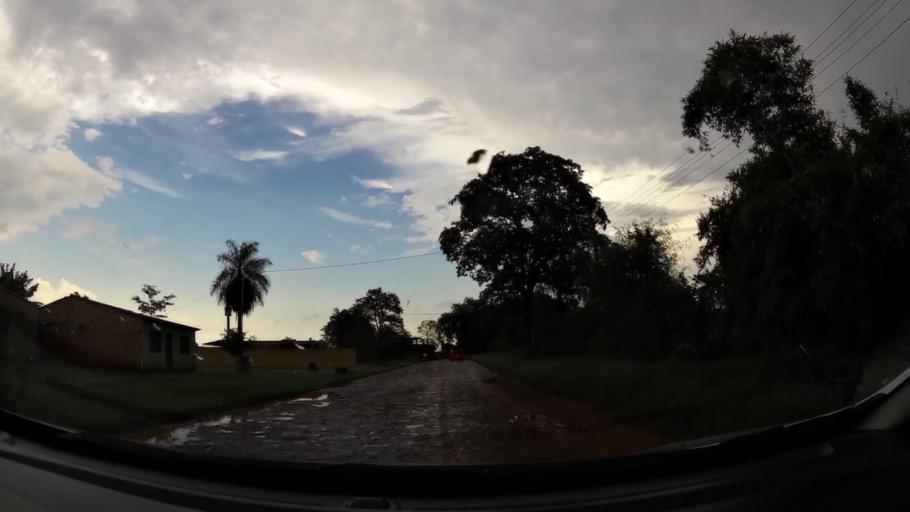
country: PY
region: Alto Parana
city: Presidente Franco
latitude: -25.5423
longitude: -54.6504
